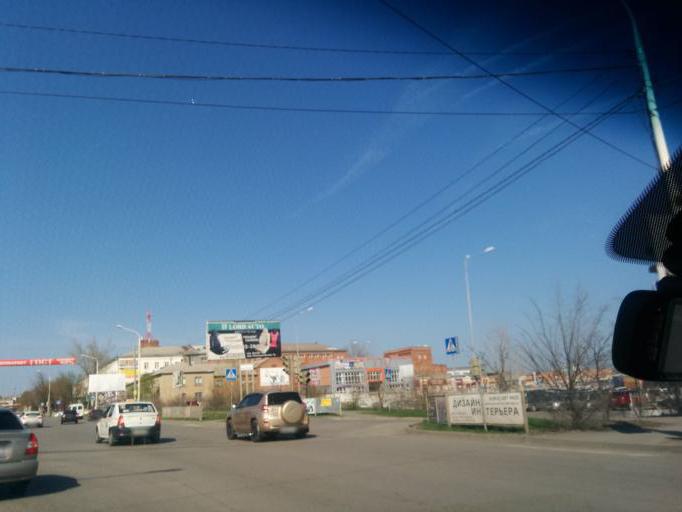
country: RU
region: Rostov
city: Shakhty
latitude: 47.6980
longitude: 40.2081
